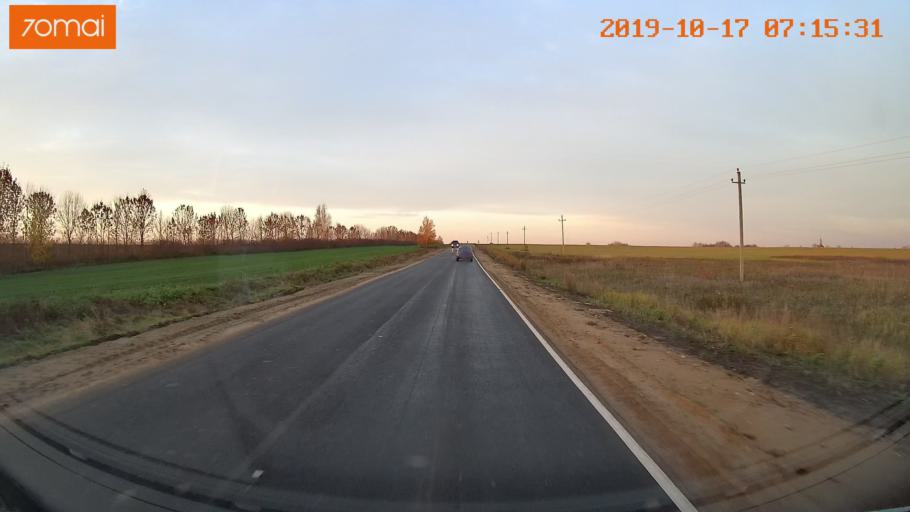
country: RU
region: Vladimir
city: Suzdal'
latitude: 56.3798
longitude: 40.2662
